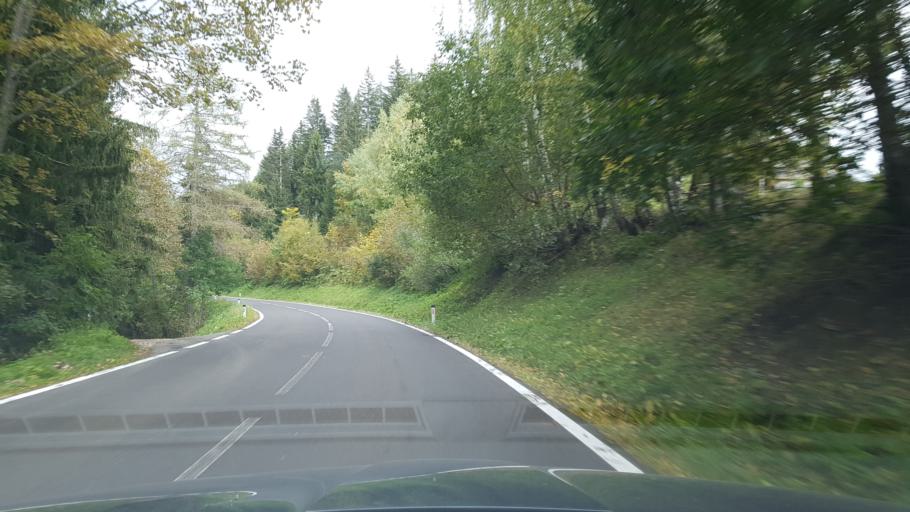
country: AT
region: Styria
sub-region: Politischer Bezirk Murtal
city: Kleinlobming
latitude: 47.1356
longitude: 14.8601
